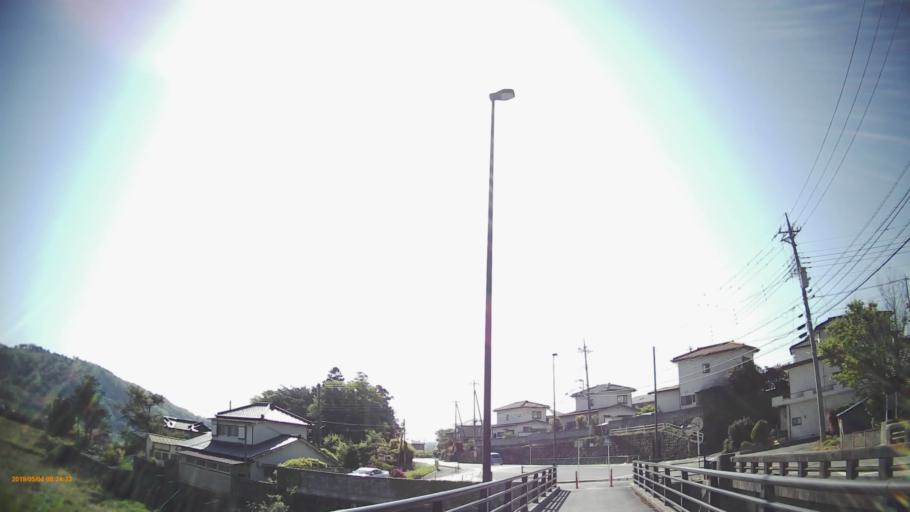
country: JP
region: Yamanashi
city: Nirasaki
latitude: 35.7321
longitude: 138.4113
